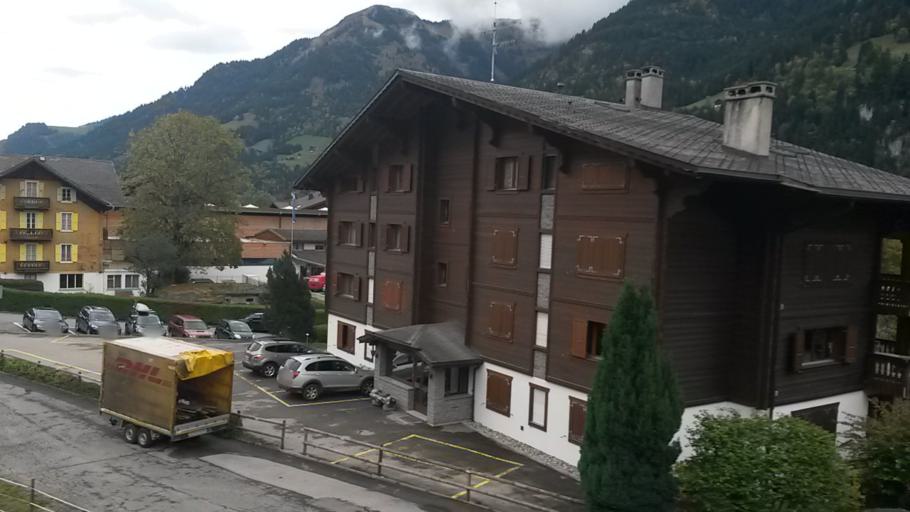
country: CH
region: Valais
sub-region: Monthey District
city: Champery
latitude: 46.1761
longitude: 6.8710
